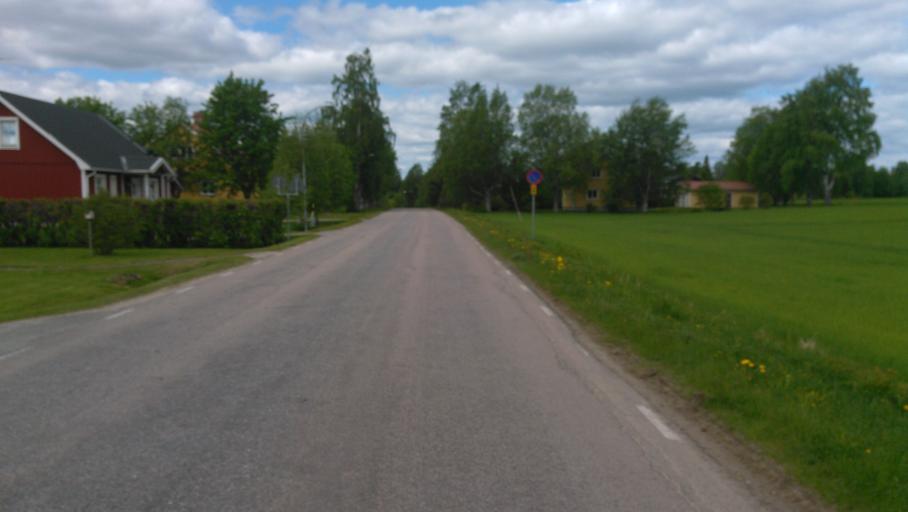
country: SE
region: Vaesterbotten
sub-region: Umea Kommun
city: Roback
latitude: 63.8685
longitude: 20.0709
